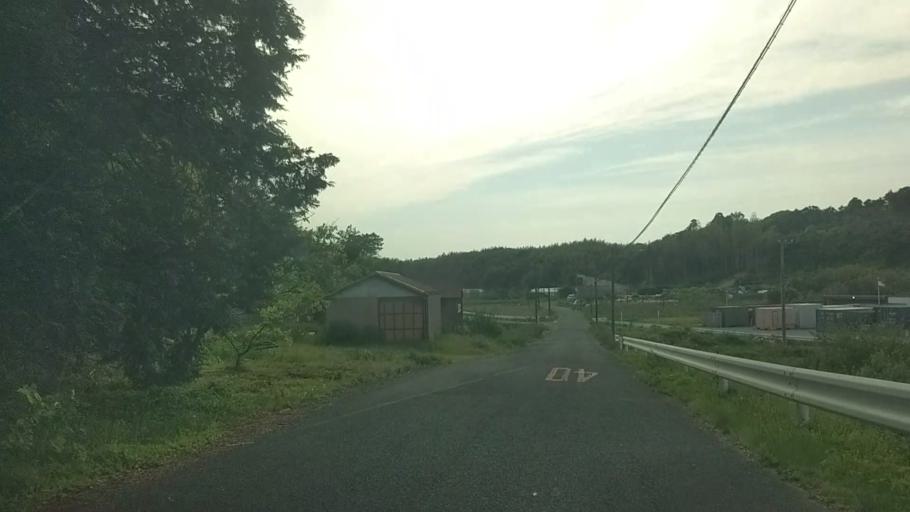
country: JP
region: Shizuoka
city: Hamamatsu
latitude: 34.7251
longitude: 137.6420
